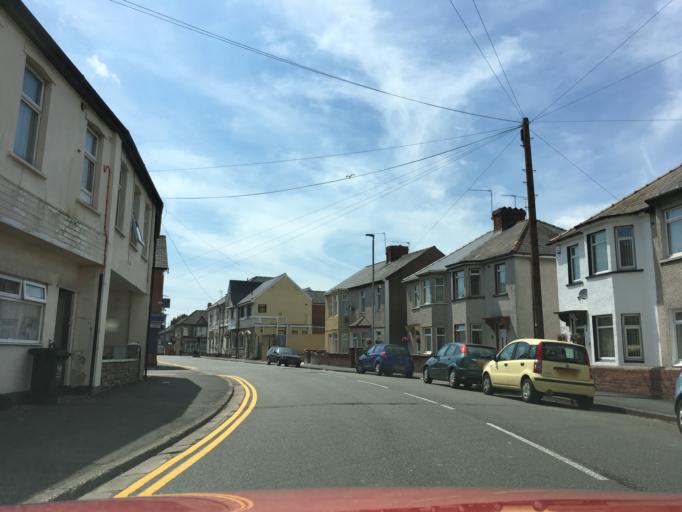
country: GB
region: Wales
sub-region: Newport
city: Newport
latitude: 51.5827
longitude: -2.9722
